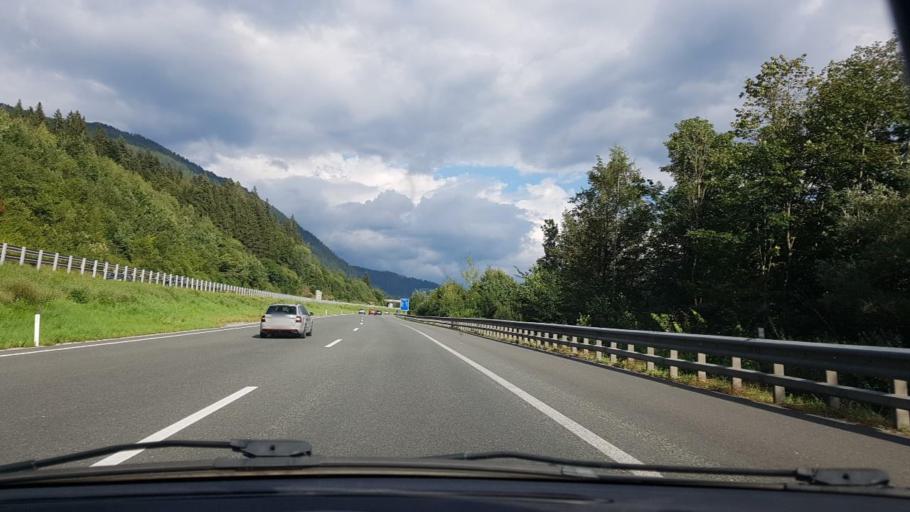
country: AT
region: Salzburg
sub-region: Politischer Bezirk Sankt Johann im Pongau
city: Werfenweng
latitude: 47.4341
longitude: 13.2474
